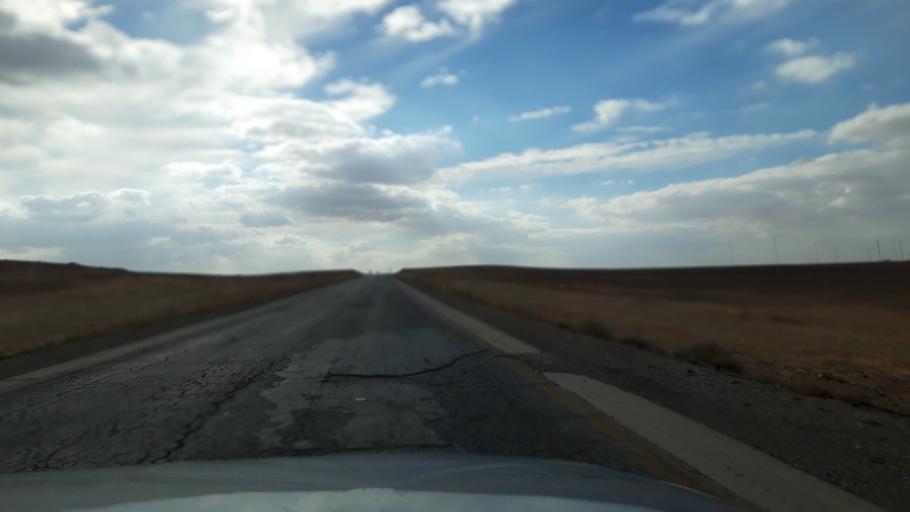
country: JO
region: Amman
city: Al Azraq ash Shamali
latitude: 31.7300
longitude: 36.4869
